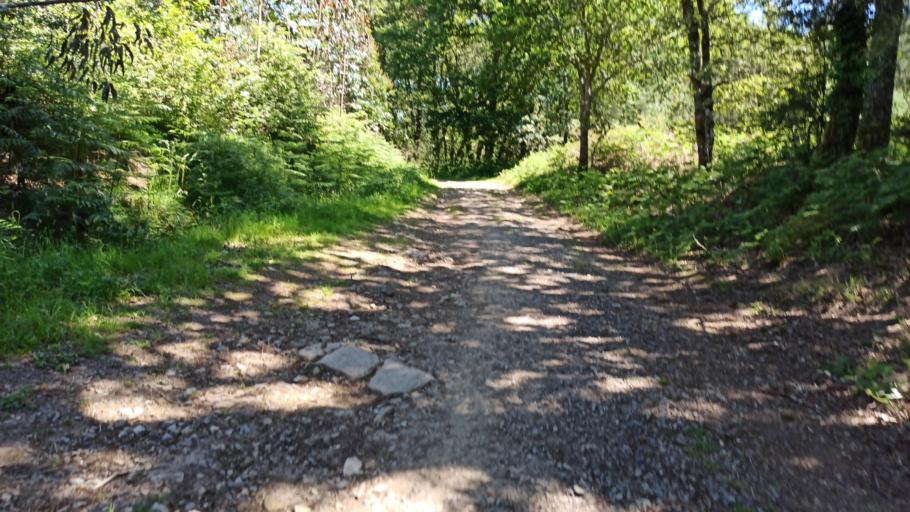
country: ES
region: Galicia
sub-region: Provincia da Coruna
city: Negreira
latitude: 42.9173
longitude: -8.7274
